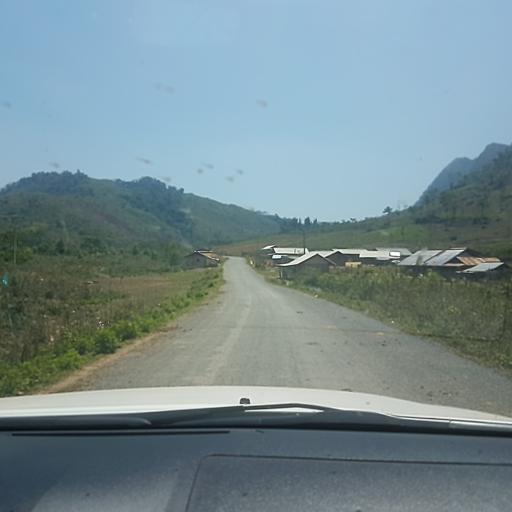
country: VN
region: Nghe An
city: Con Cuong
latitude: 18.5921
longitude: 104.6377
